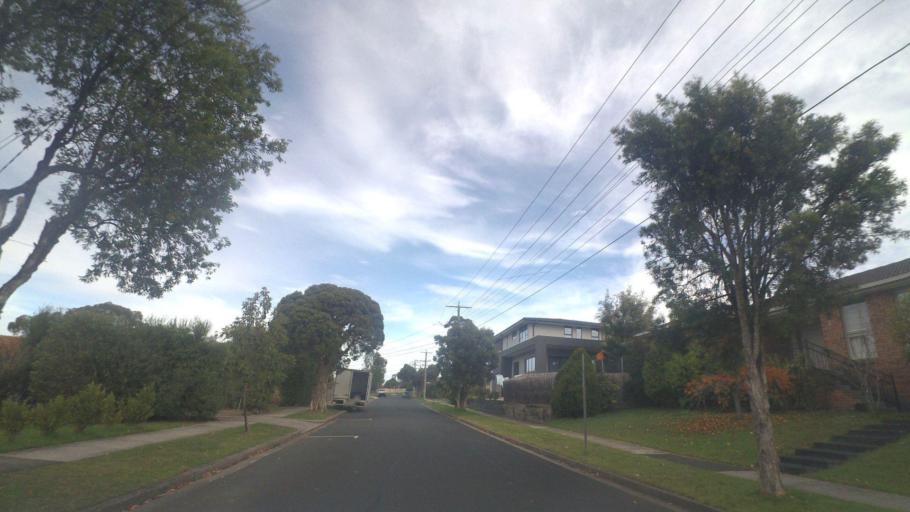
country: AU
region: Victoria
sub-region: Whitehorse
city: Vermont South
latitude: -37.8611
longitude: 145.1740
